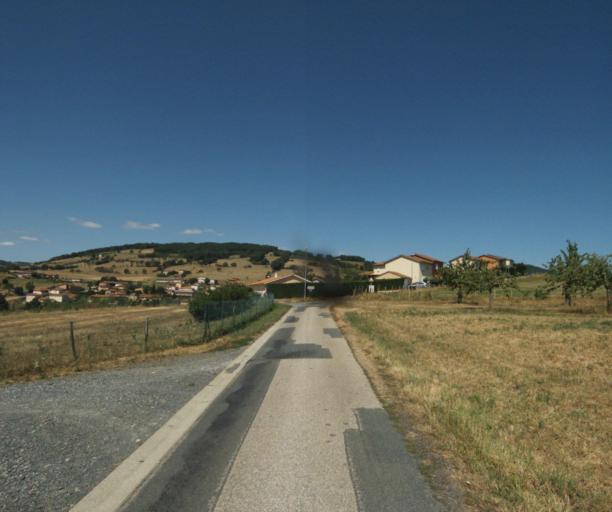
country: FR
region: Rhone-Alpes
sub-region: Departement du Rhone
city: Bessenay
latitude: 45.7965
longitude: 4.5515
